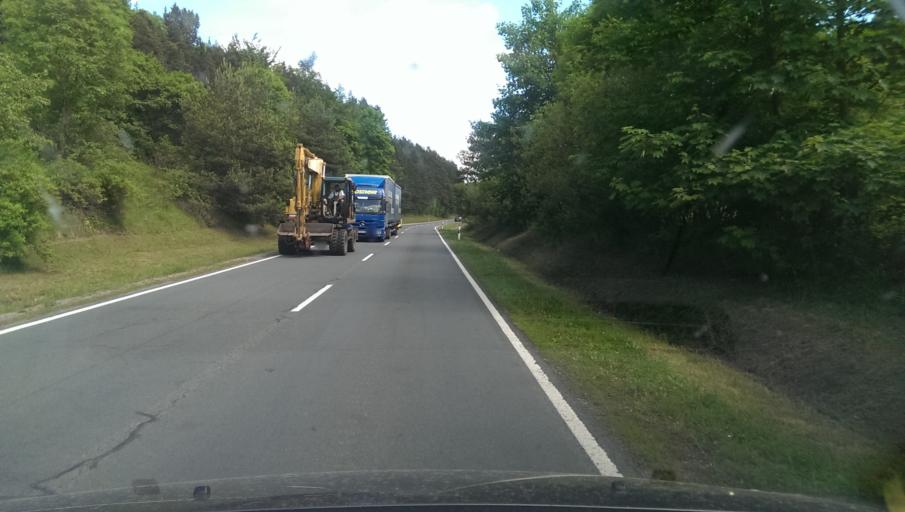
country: DE
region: Thuringia
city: Geschwenda
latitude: 50.7424
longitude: 10.8202
